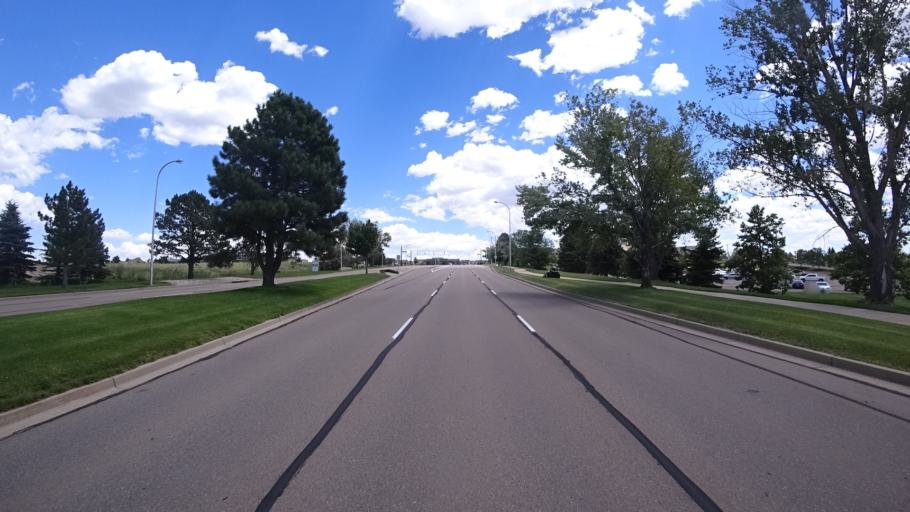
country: US
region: Colorado
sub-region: El Paso County
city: Air Force Academy
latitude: 38.9605
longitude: -104.7868
